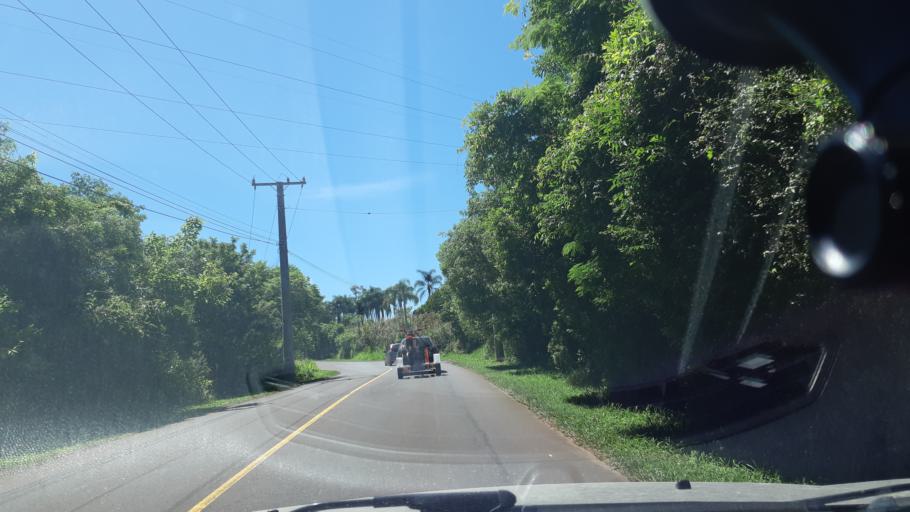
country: BR
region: Rio Grande do Sul
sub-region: Ivoti
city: Ivoti
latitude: -29.6210
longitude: -51.1135
